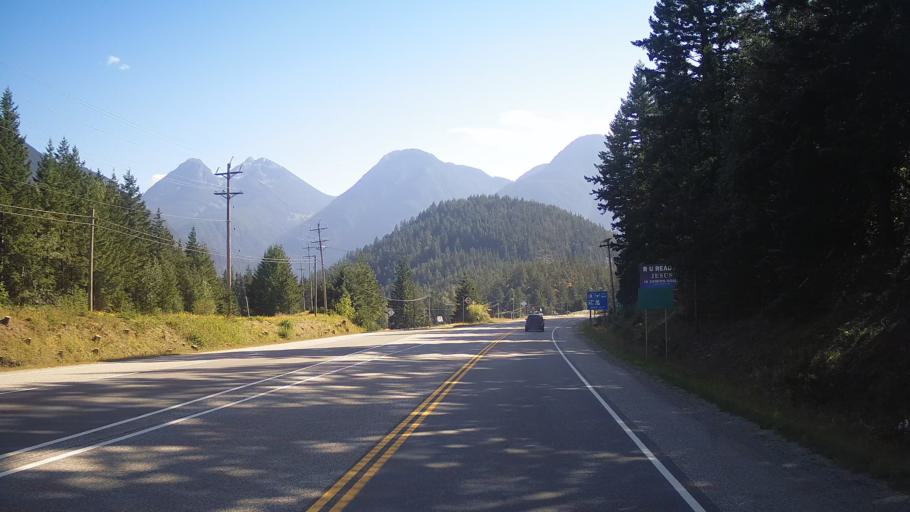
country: CA
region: British Columbia
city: Hope
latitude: 49.3954
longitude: -121.4578
